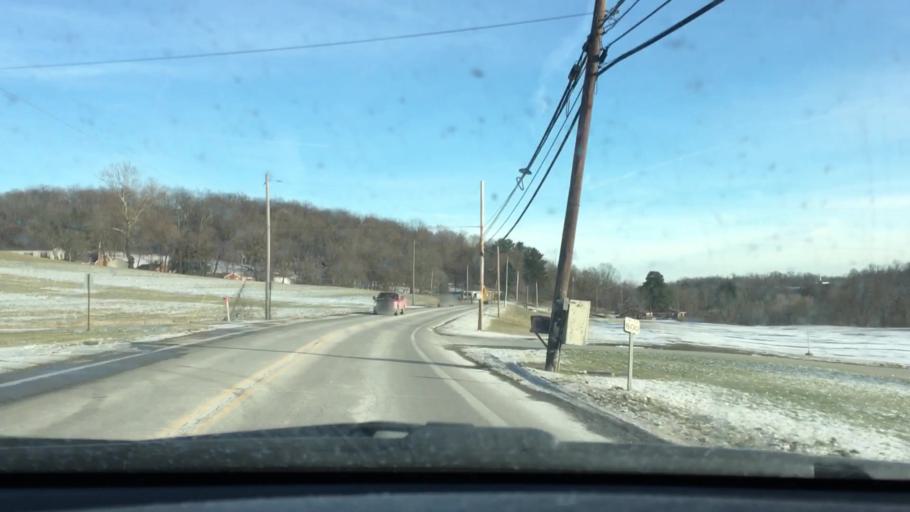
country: US
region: Pennsylvania
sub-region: Washington County
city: Gastonville
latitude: 40.2764
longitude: -80.0288
